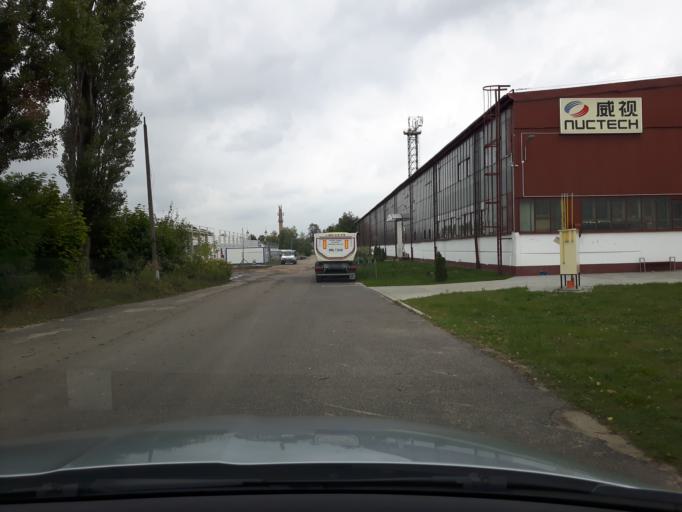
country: PL
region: Masovian Voivodeship
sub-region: Powiat wolominski
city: Kobylka
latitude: 52.3306
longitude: 21.1944
